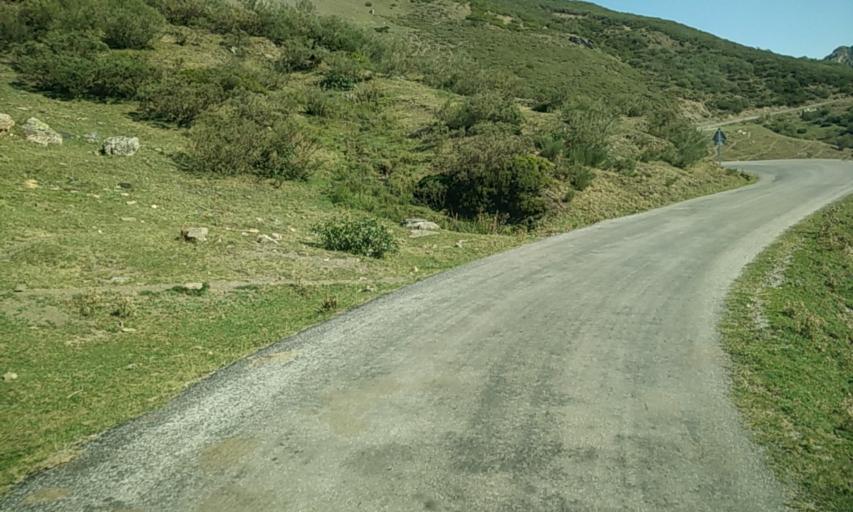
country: ES
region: Cantabria
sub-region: Provincia de Cantabria
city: Camaleno
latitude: 43.0726
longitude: -4.7577
